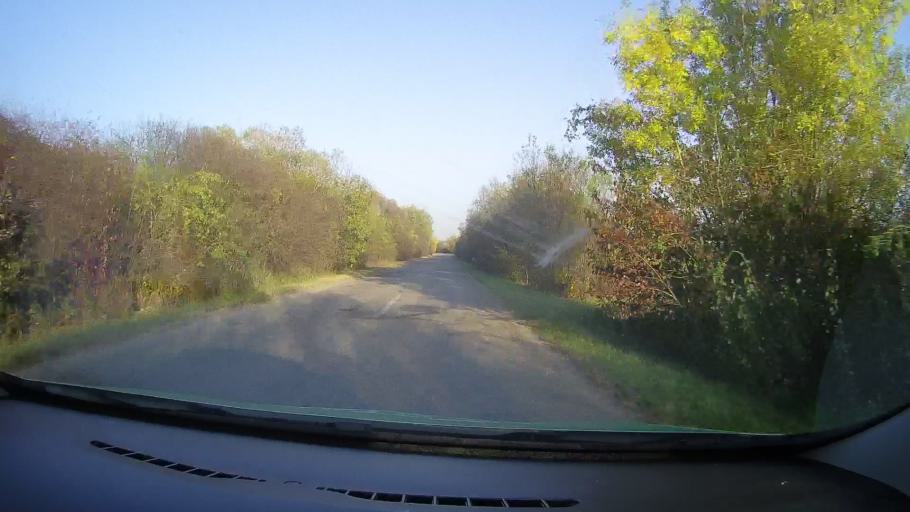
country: RO
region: Arad
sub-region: Comuna Silindia
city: Silindia
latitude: 46.3363
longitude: 21.8952
